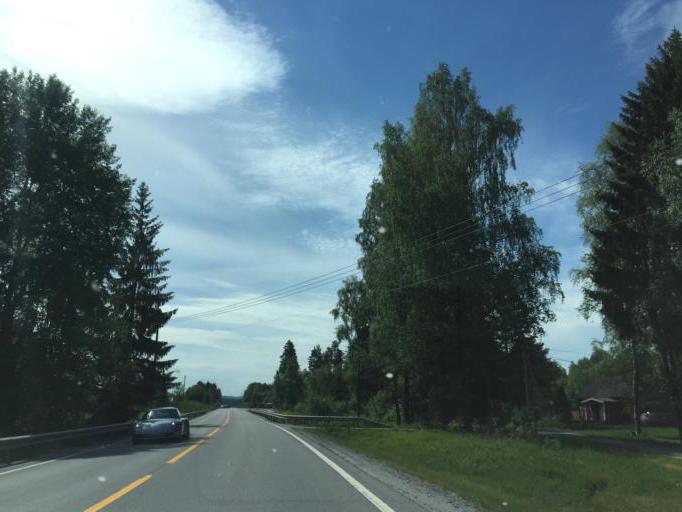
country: NO
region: Hedmark
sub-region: Sor-Odal
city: Skarnes
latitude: 60.2453
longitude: 11.6680
